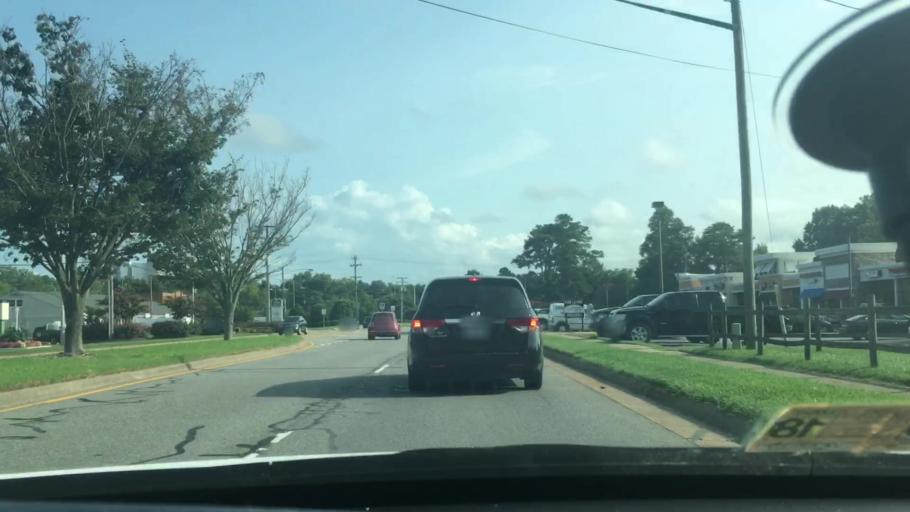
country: US
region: Virginia
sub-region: City of Virginia Beach
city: Virginia Beach
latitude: 36.8495
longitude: -75.9944
